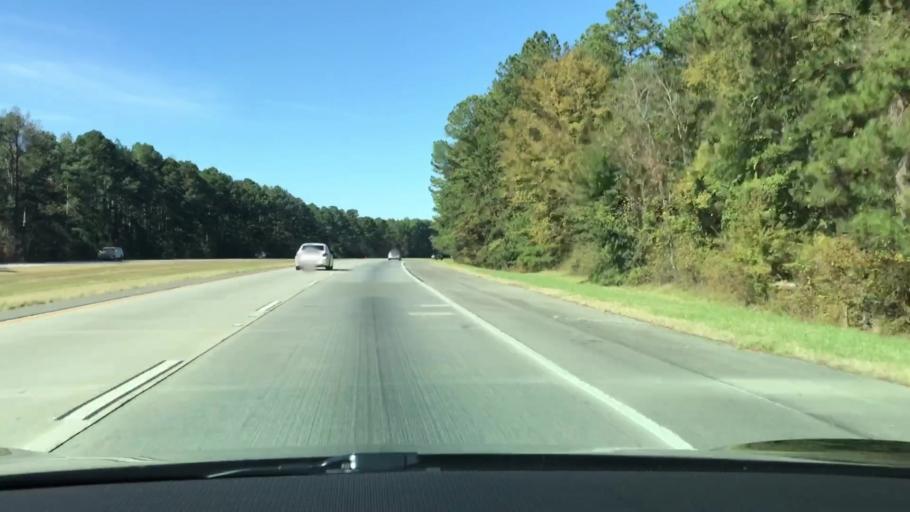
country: US
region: Georgia
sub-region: Taliaferro County
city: Crawfordville
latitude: 33.5322
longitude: -82.9848
